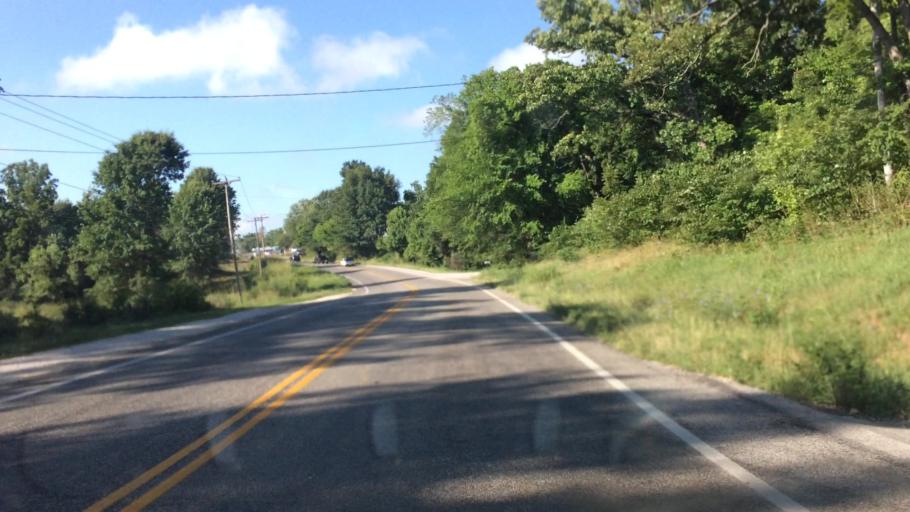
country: US
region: Missouri
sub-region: Greene County
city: Springfield
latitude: 37.2735
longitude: -93.2641
